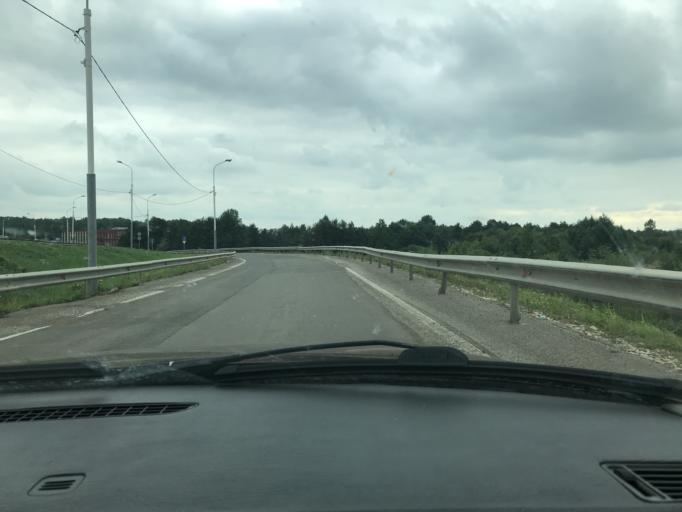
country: RU
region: Kaluga
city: Kaluga
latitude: 54.5544
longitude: 36.3352
